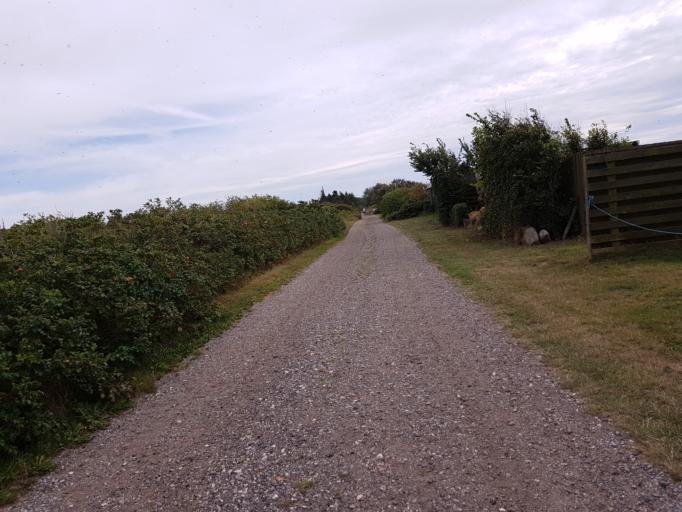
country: DK
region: Zealand
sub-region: Guldborgsund Kommune
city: Nykobing Falster
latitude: 54.5871
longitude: 11.9225
